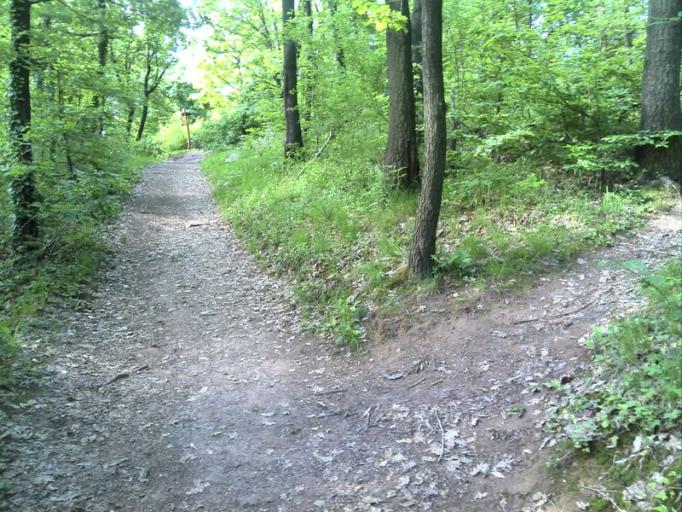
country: HU
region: Baranya
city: Pecs
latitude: 46.0887
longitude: 18.1786
